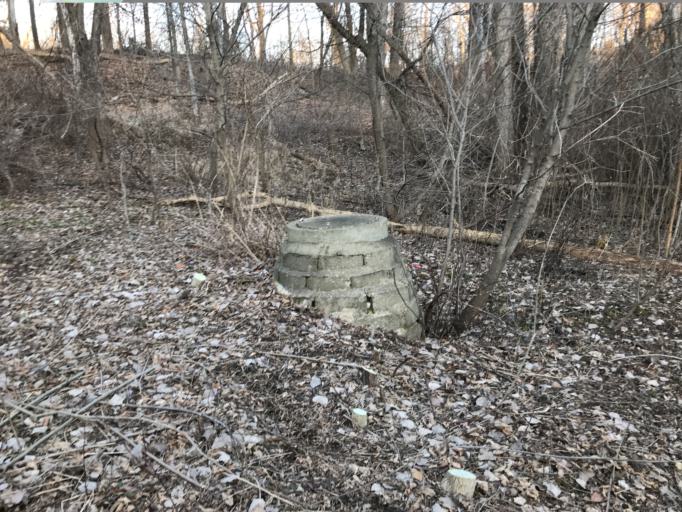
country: US
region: Michigan
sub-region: Eaton County
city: Waverly
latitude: 42.6974
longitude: -84.6226
